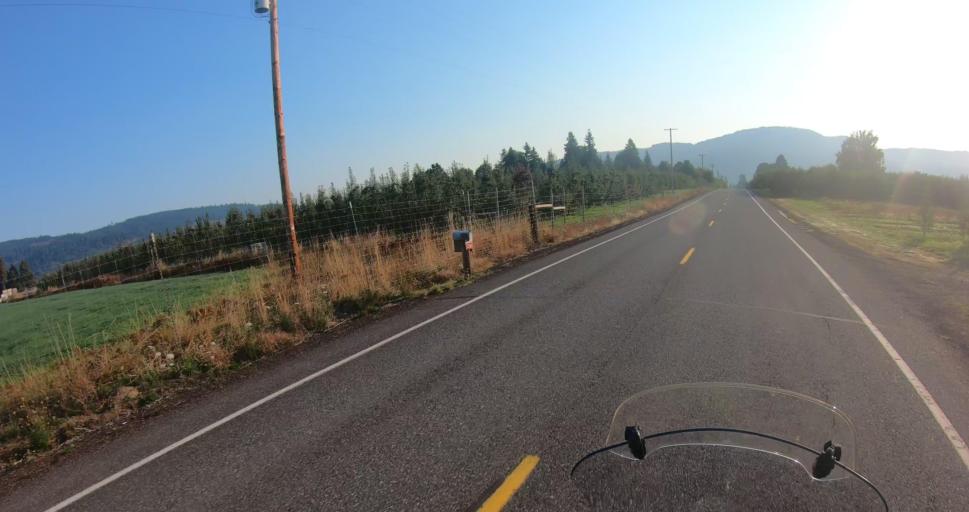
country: US
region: Oregon
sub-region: Hood River County
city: Odell
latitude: 45.5421
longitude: -121.5971
